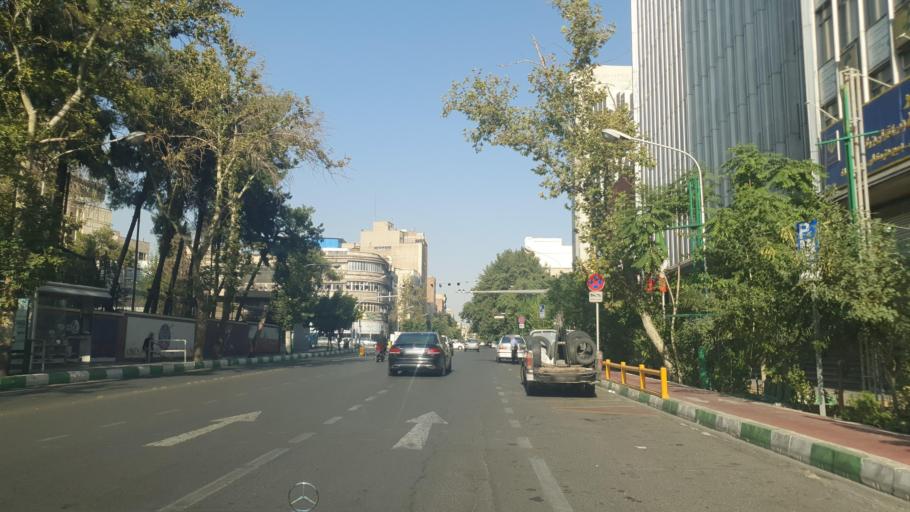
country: IR
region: Tehran
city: Tehran
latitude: 35.7069
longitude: 51.4245
